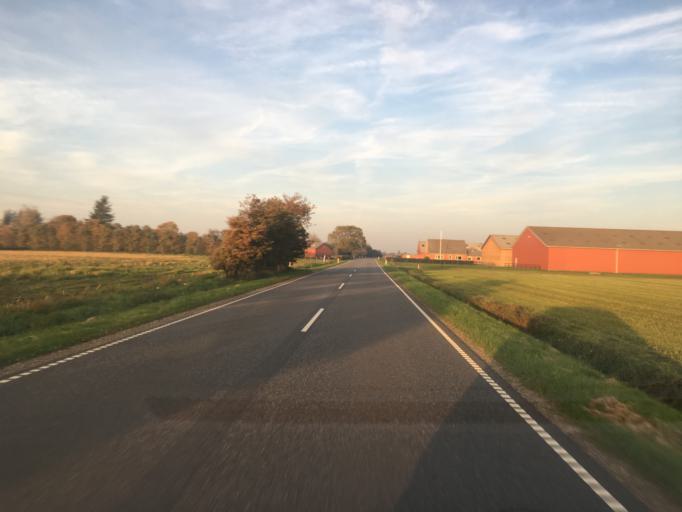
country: DK
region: South Denmark
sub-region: Tonder Kommune
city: Logumkloster
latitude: 55.0442
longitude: 9.0363
